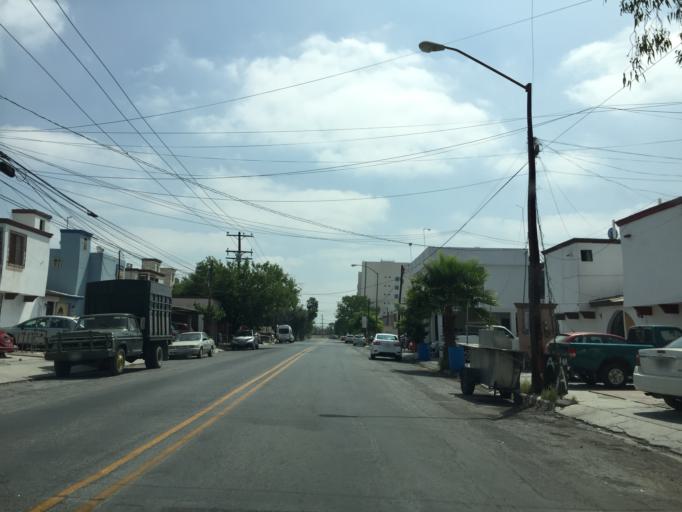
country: MX
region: Nuevo Leon
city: Guadalupe
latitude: 25.7065
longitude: -100.2272
